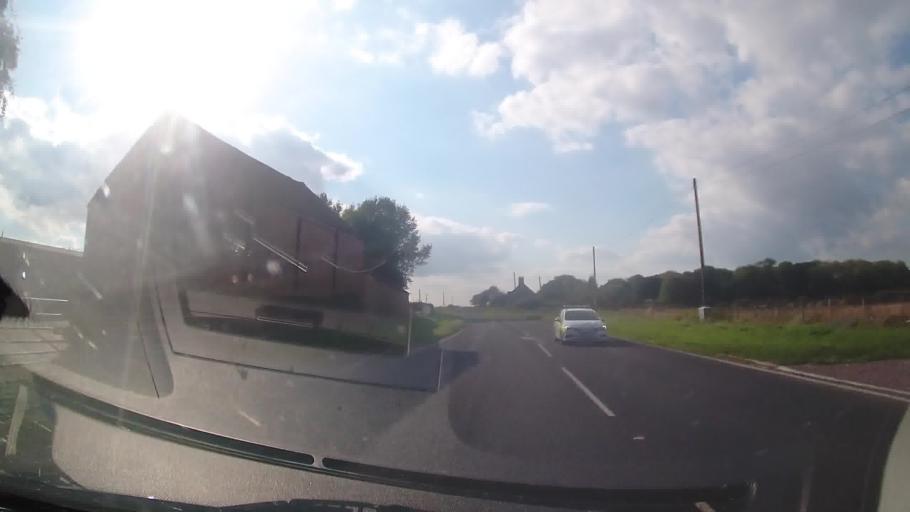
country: GB
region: England
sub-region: Kent
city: Hythe
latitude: 51.0930
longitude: 1.0829
